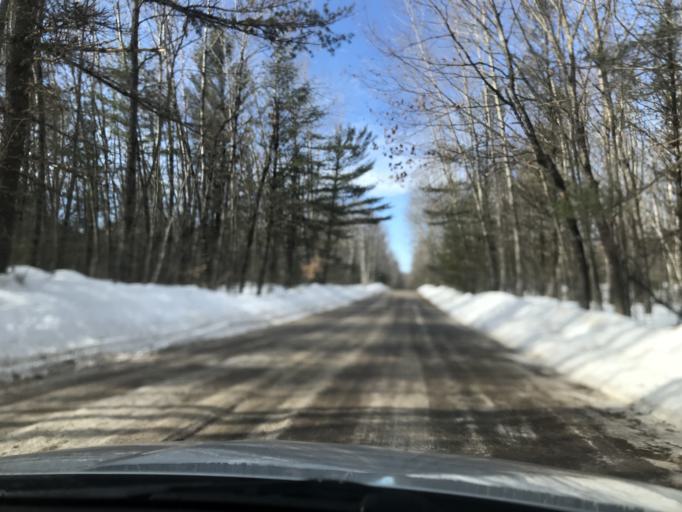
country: US
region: Wisconsin
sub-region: Menominee County
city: Legend Lake
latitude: 45.1129
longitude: -88.4361
